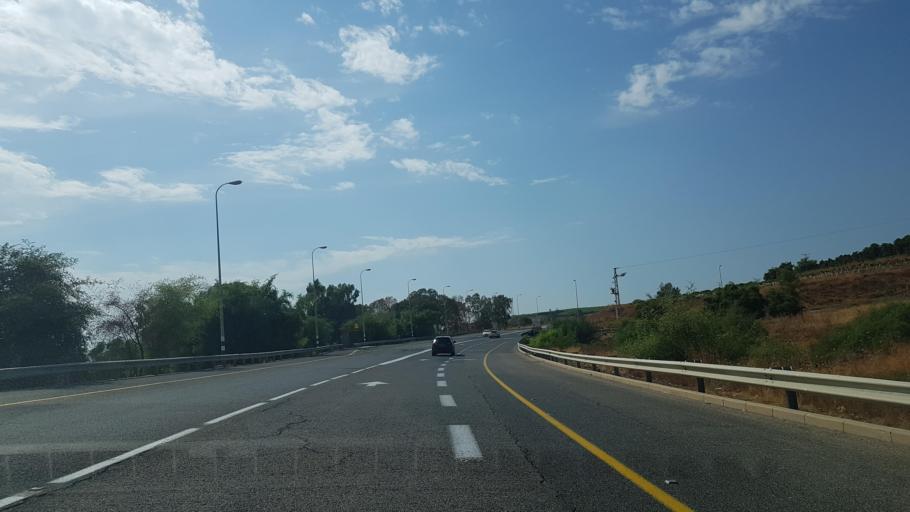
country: SY
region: Quneitra
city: Al Butayhah
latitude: 32.8941
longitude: 35.5998
